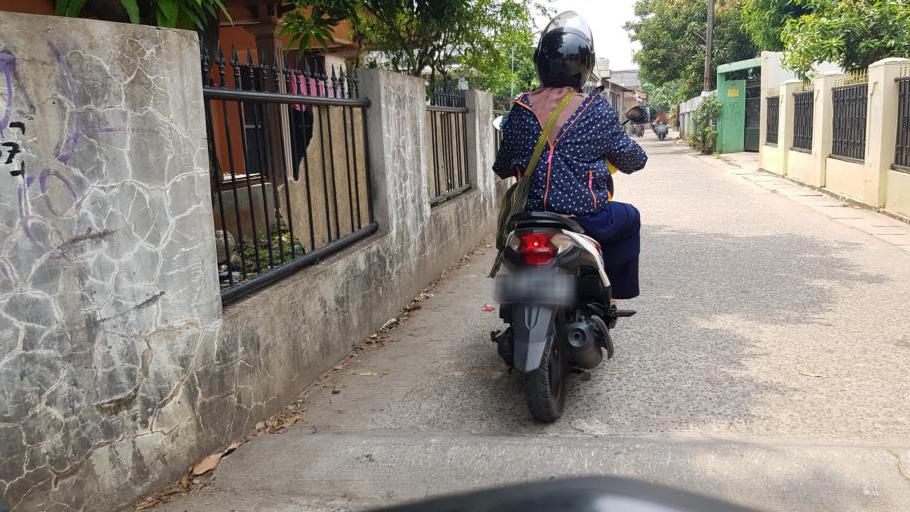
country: ID
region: West Java
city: Pamulang
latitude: -6.3311
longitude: 106.7983
